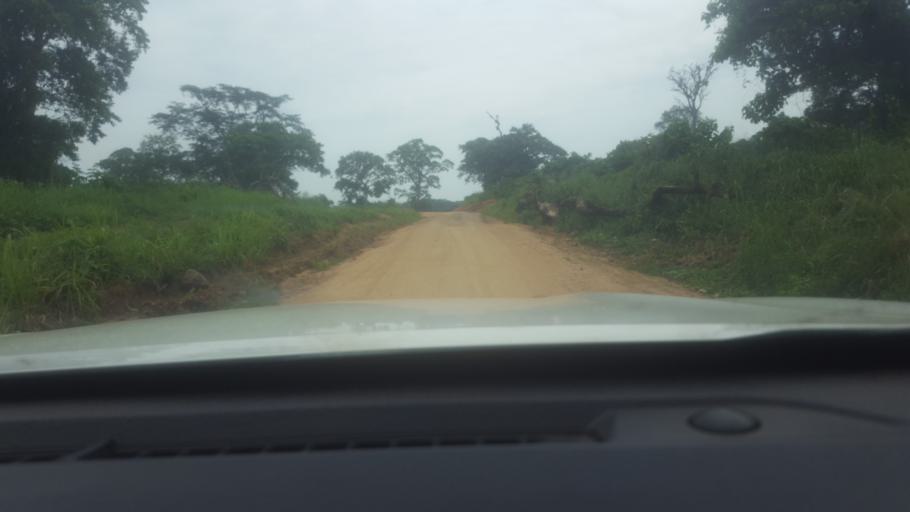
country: ET
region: Southern Nations, Nationalities, and People's Region
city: Tippi
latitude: 7.4096
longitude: 35.0728
